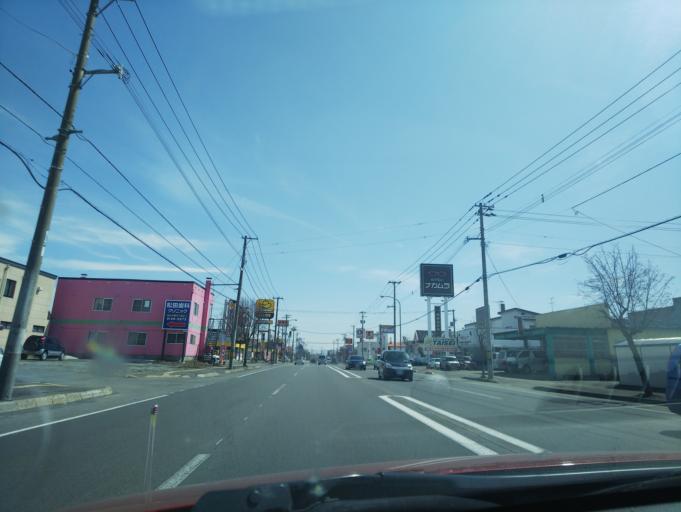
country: JP
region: Hokkaido
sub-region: Asahikawa-shi
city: Asahikawa
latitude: 43.7848
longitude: 142.4118
